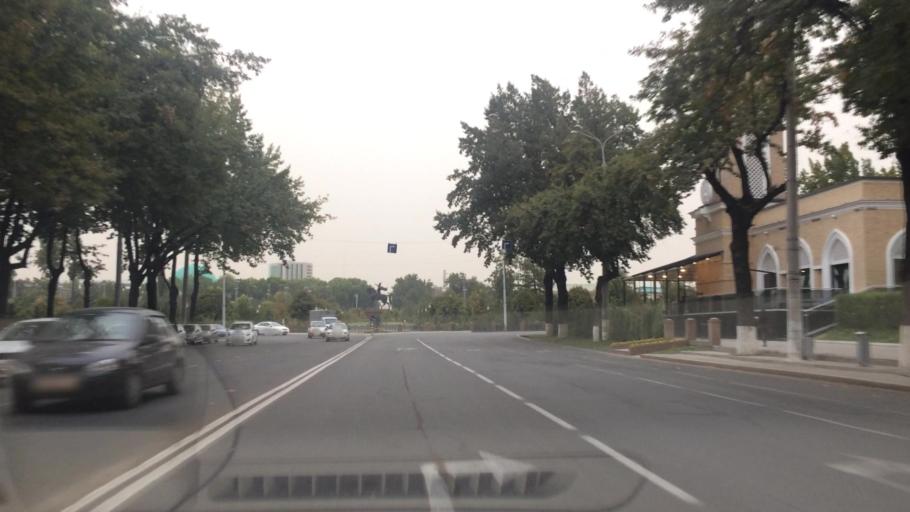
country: UZ
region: Toshkent Shahri
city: Tashkent
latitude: 41.3091
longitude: 69.2794
